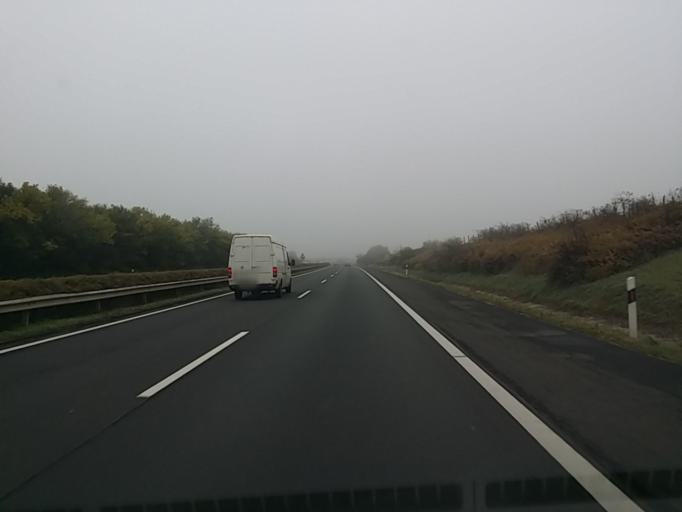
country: HU
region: Heves
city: Nagyrede
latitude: 47.7196
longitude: 19.8389
